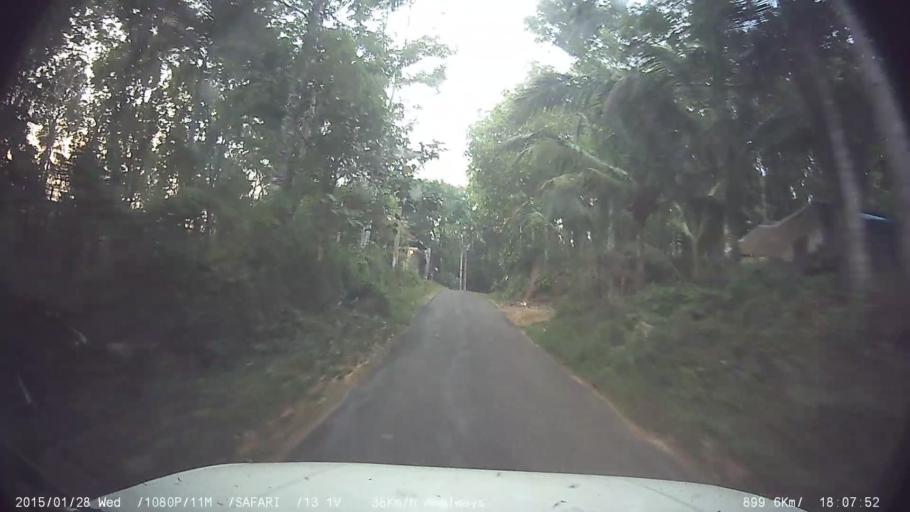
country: IN
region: Kerala
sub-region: Kottayam
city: Palackattumala
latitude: 9.7369
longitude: 76.5764
